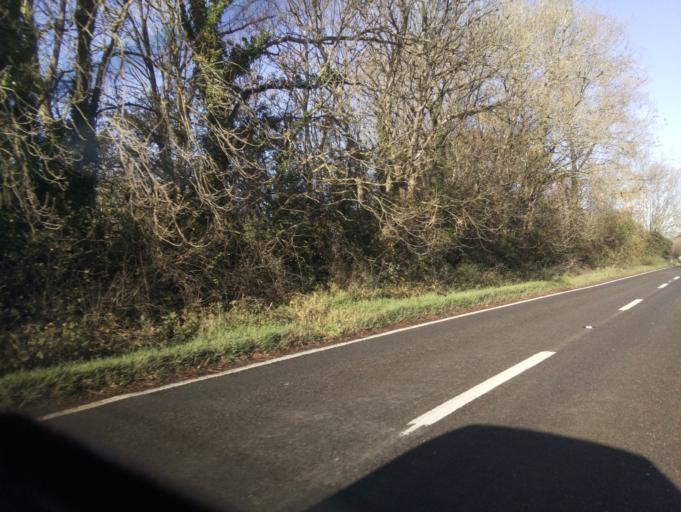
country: GB
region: England
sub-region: Somerset
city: Westonzoyland
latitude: 51.1173
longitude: -2.9640
